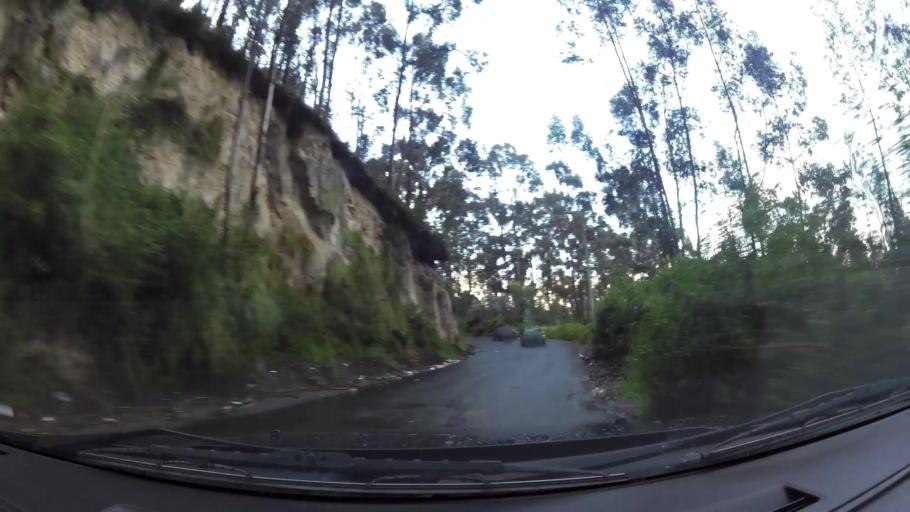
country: EC
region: Pichincha
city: Quito
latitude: -0.1102
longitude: -78.5218
